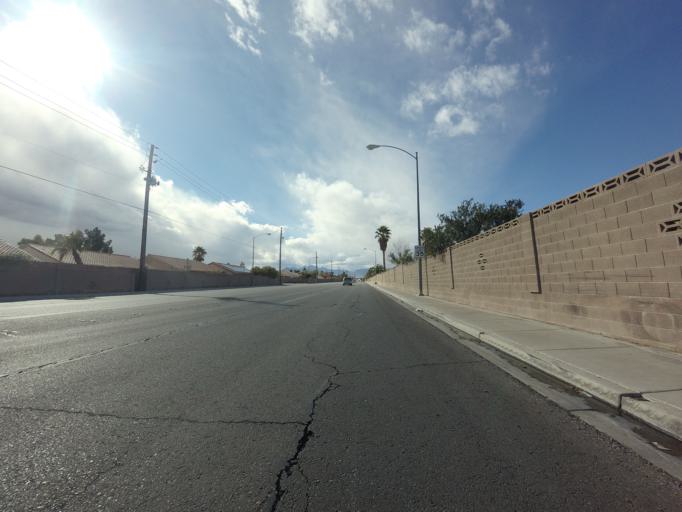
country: US
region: Nevada
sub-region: Clark County
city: North Las Vegas
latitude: 36.2543
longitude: -115.1447
